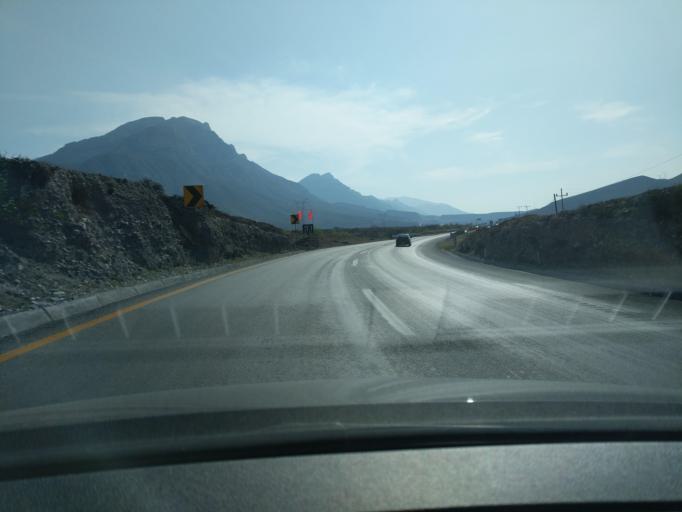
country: MX
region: Nuevo Leon
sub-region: Garcia
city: Las Torres de Guadalupe
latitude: 25.6639
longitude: -100.7072
